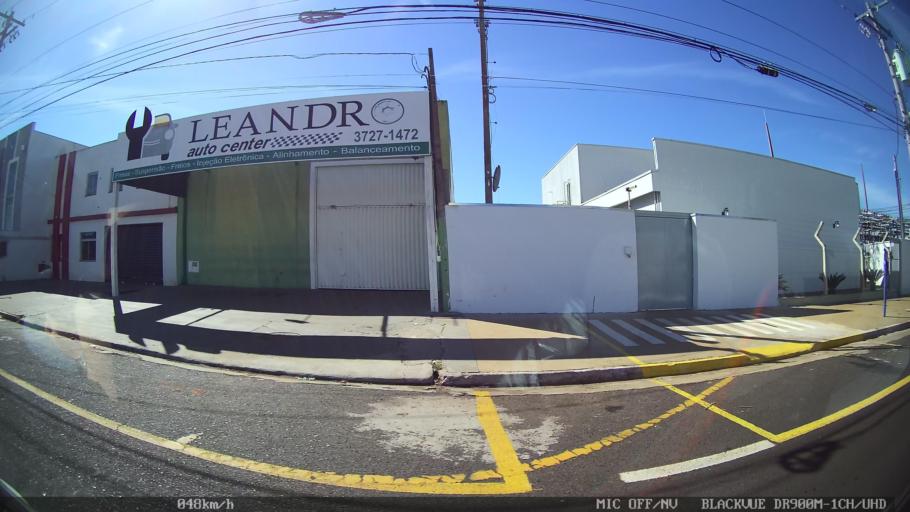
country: BR
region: Sao Paulo
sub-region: Franca
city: Franca
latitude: -20.5454
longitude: -47.3741
